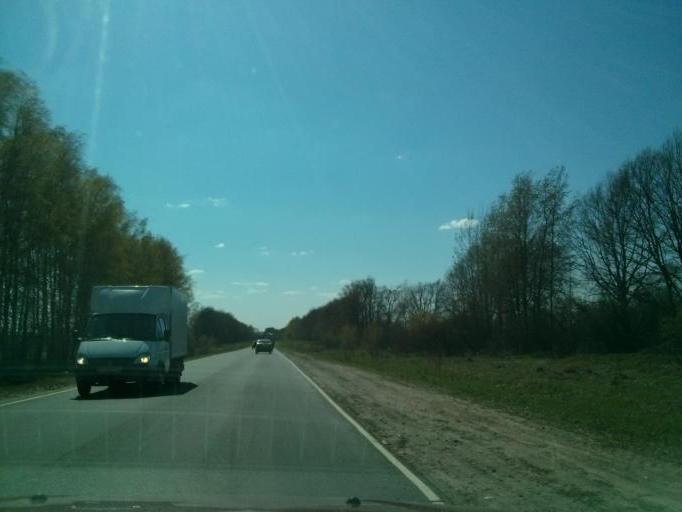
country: RU
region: Nizjnij Novgorod
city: Bogorodsk
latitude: 56.0568
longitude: 43.4126
